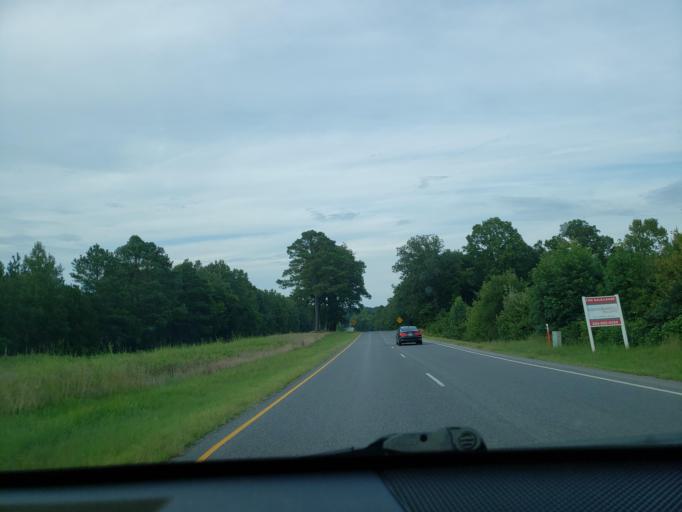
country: US
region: Virginia
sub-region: Brunswick County
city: Lawrenceville
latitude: 36.7378
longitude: -77.8982
